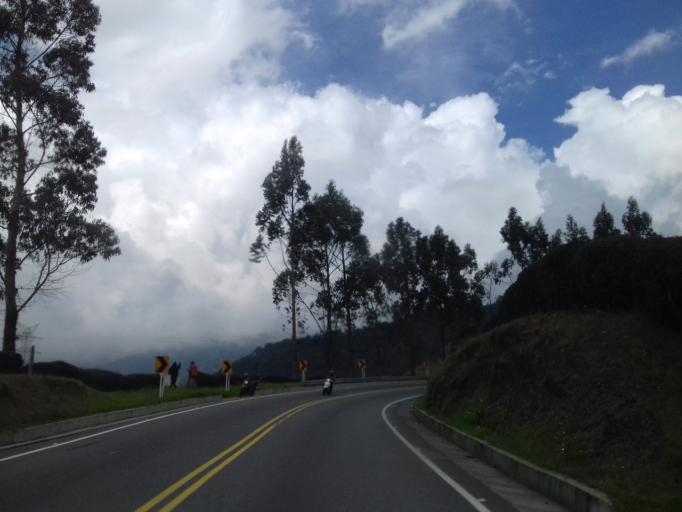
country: CO
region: Caldas
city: Villamaria
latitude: 5.0209
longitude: -75.3663
